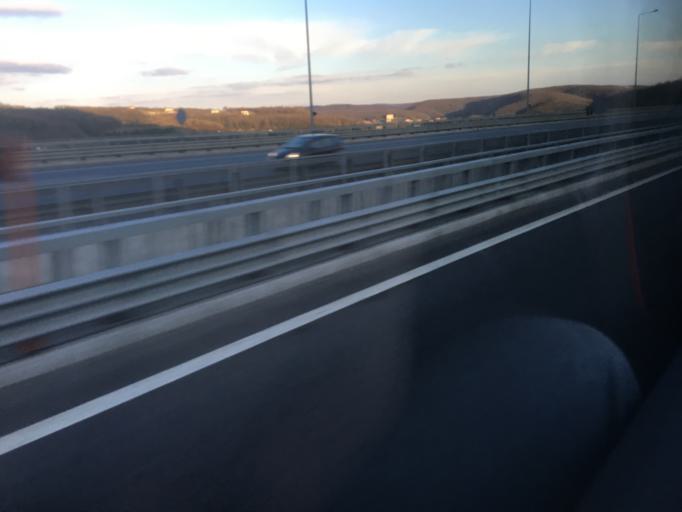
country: TR
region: Istanbul
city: Mahmut Sevket Pasa
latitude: 41.1412
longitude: 29.2840
